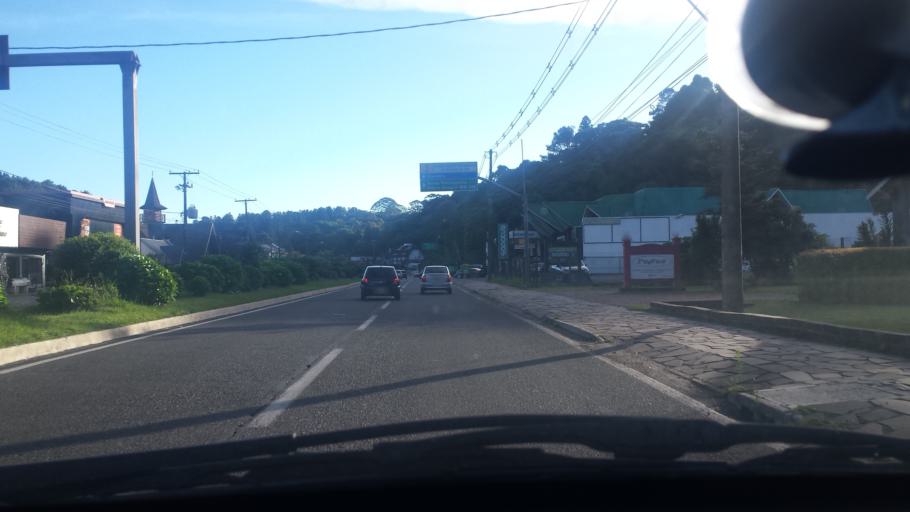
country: BR
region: Rio Grande do Sul
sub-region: Canela
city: Canela
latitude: -29.3700
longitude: -50.8622
